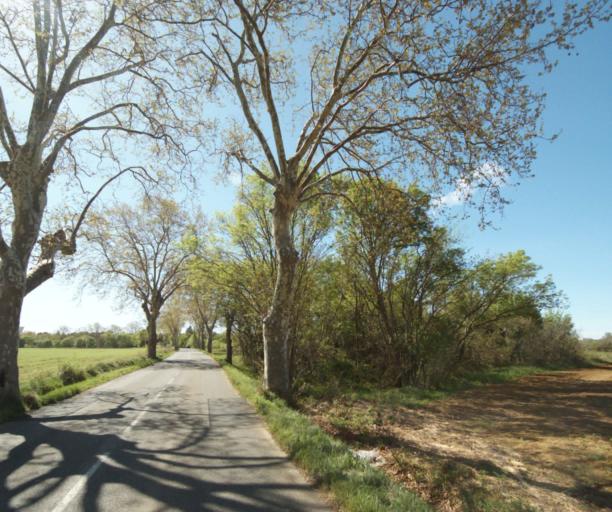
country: FR
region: Languedoc-Roussillon
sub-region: Departement de l'Herault
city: Villeneuve-les-Maguelone
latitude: 43.5484
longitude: 3.8467
